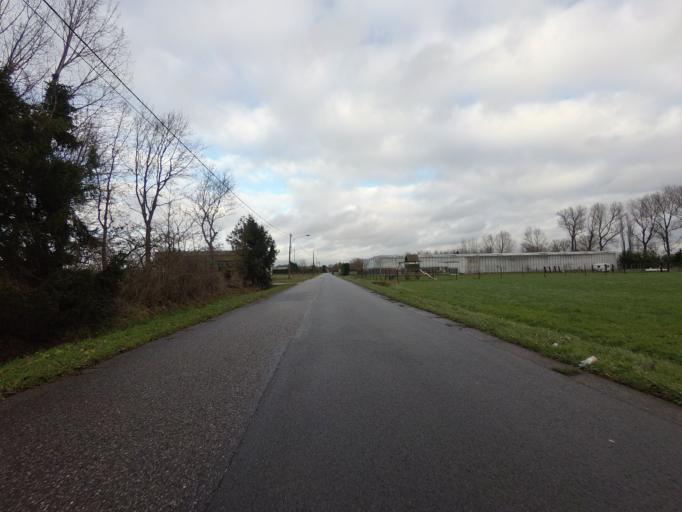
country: BE
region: Flanders
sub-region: Provincie Antwerpen
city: Lier
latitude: 51.1001
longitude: 4.5645
